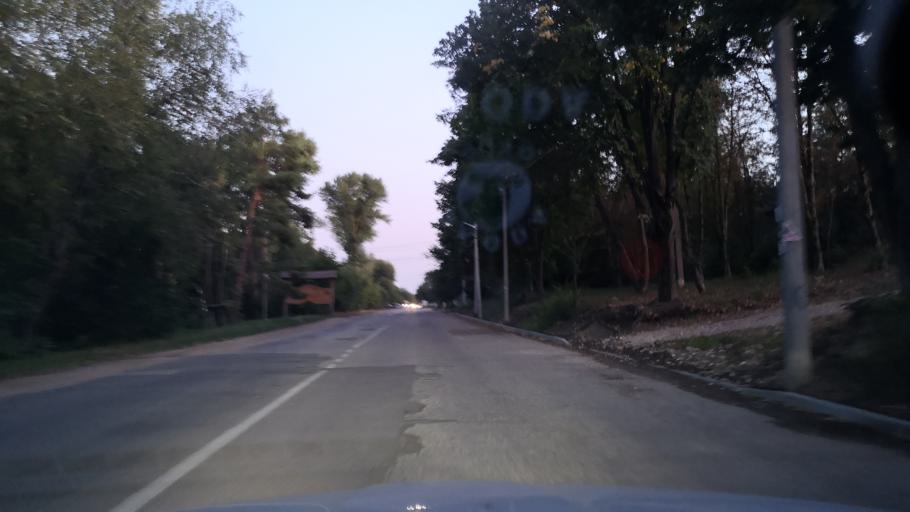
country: MD
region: Orhei
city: Orhei
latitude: 47.3940
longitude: 28.8218
